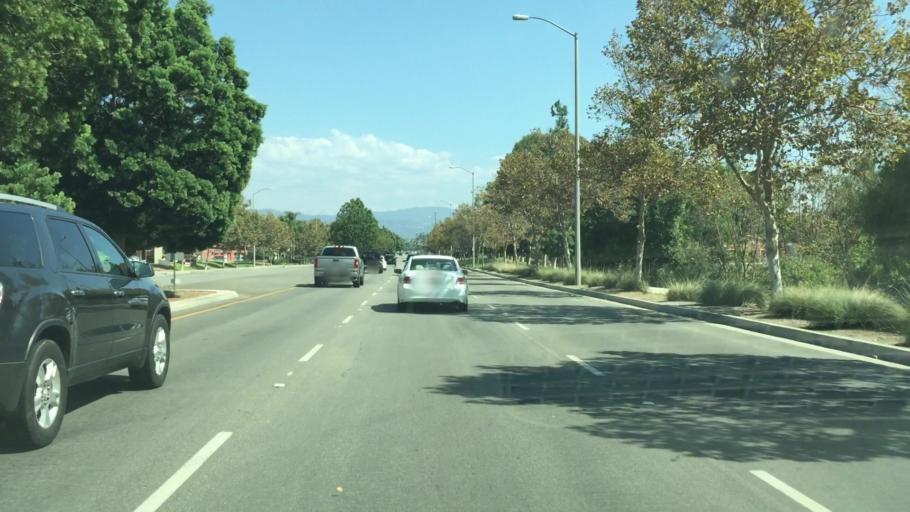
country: US
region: California
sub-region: Orange County
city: Yorba Linda
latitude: 33.9015
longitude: -117.8363
